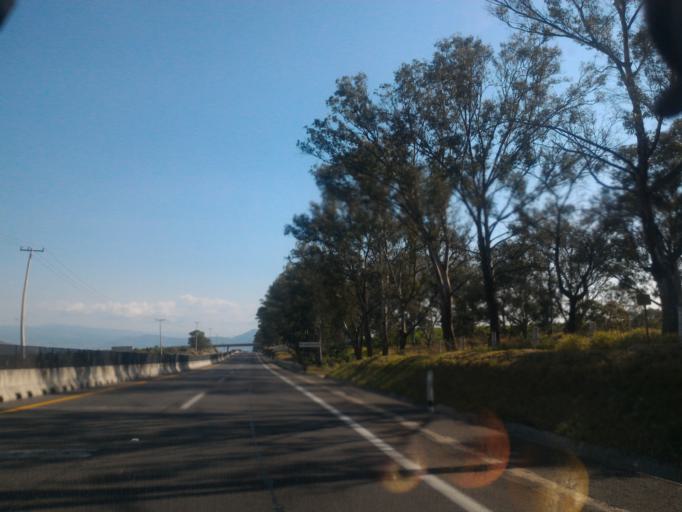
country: MX
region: Jalisco
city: Zapotiltic
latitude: 19.5995
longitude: -103.4546
